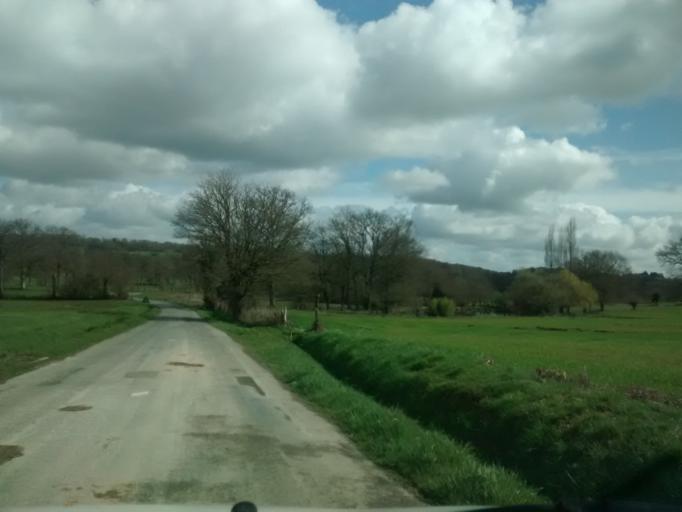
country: FR
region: Brittany
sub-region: Departement d'Ille-et-Vilaine
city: Livre-sur-Changeon
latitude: 48.1983
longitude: -1.3649
